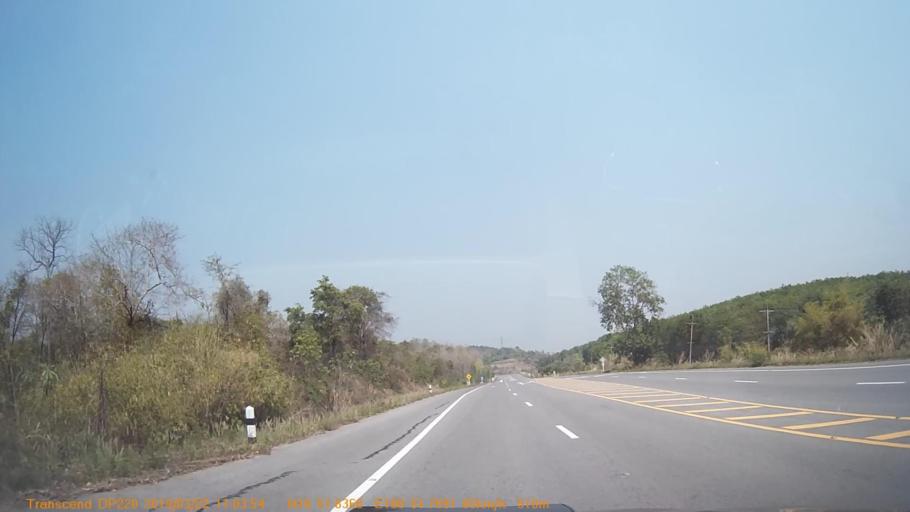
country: TH
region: Phitsanulok
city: Nakhon Thai
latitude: 16.8609
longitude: 100.8627
